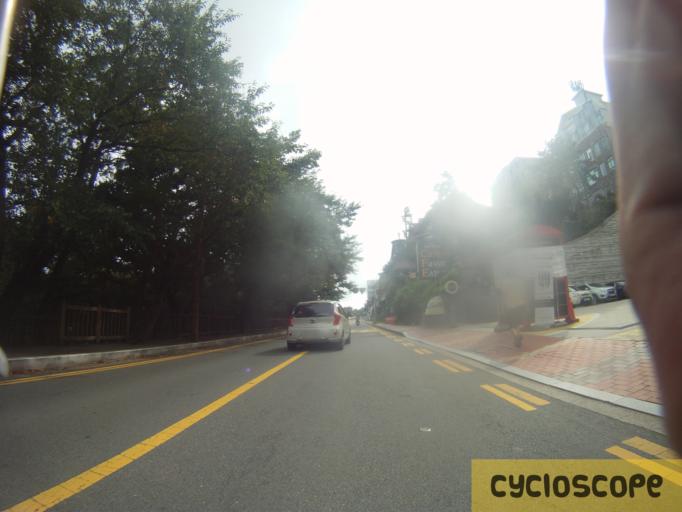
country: KR
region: Busan
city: Kijang
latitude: 35.1580
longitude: 129.1825
